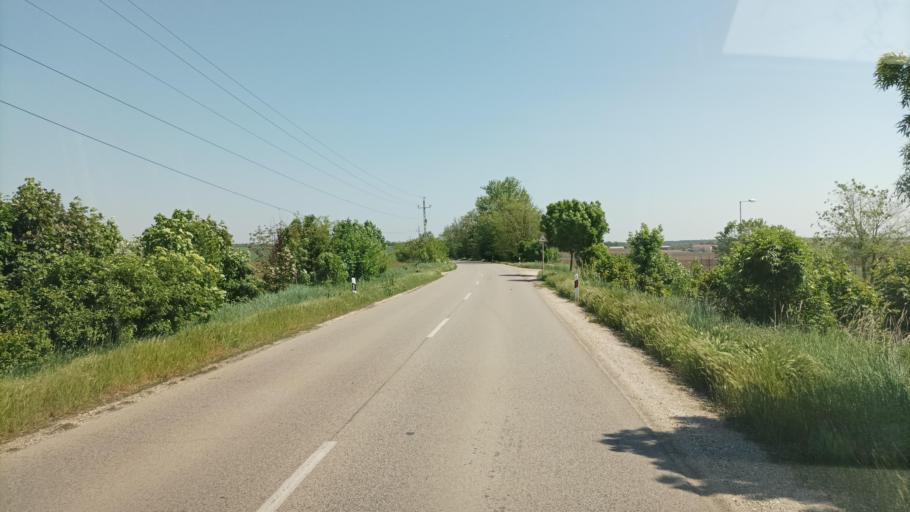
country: HU
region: Pest
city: Uri
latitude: 47.4250
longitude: 19.5245
